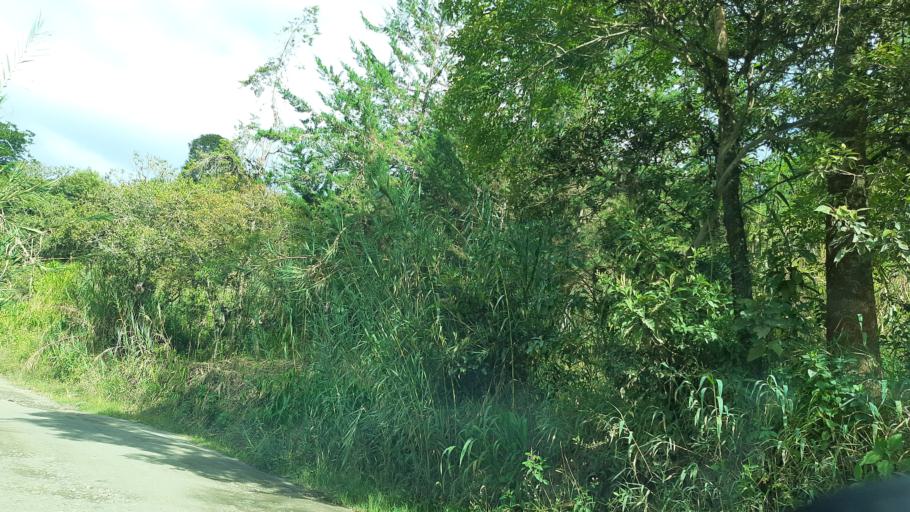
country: CO
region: Cundinamarca
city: Tenza
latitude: 5.0563
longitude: -73.4172
